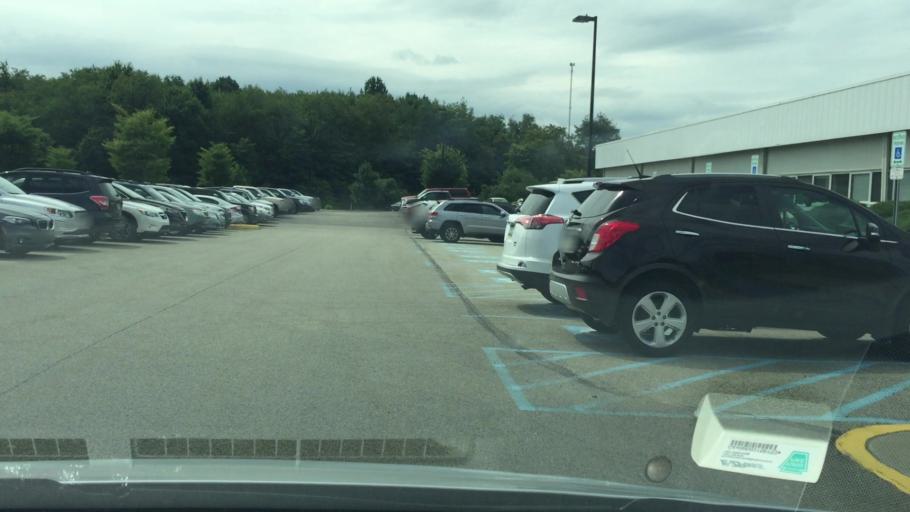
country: US
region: Pennsylvania
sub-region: Armstrong County
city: Apollo
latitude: 40.5315
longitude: -79.6495
